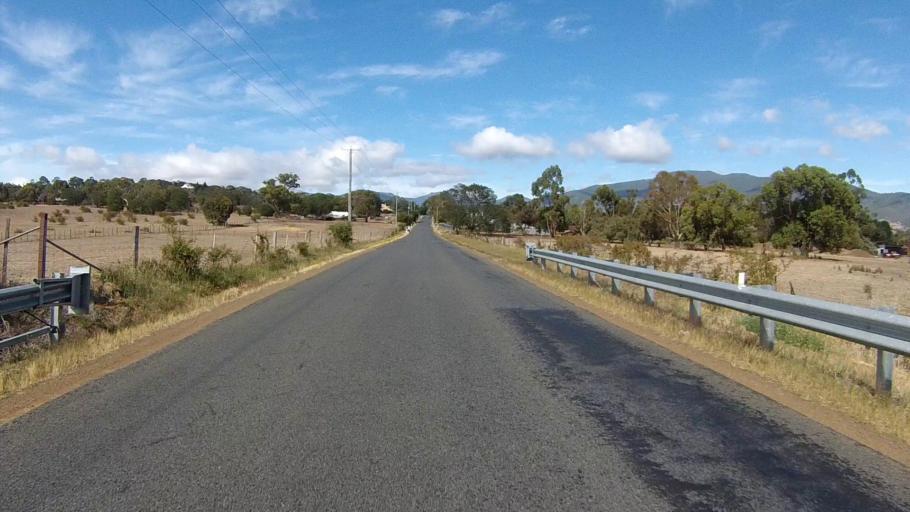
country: AU
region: Tasmania
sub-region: Brighton
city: Old Beach
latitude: -42.7651
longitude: 147.2764
